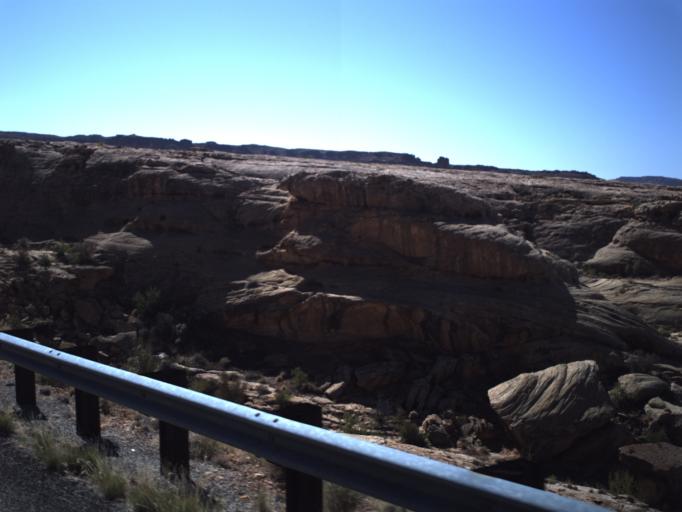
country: US
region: Utah
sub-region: San Juan County
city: Blanding
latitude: 37.9046
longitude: -110.3800
